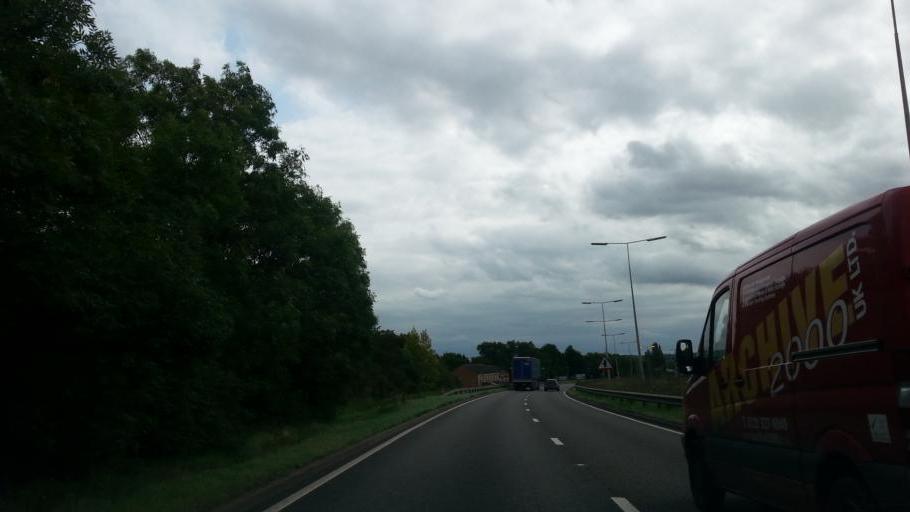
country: GB
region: England
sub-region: Northamptonshire
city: Hardingstone
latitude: 52.2078
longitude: -0.8920
